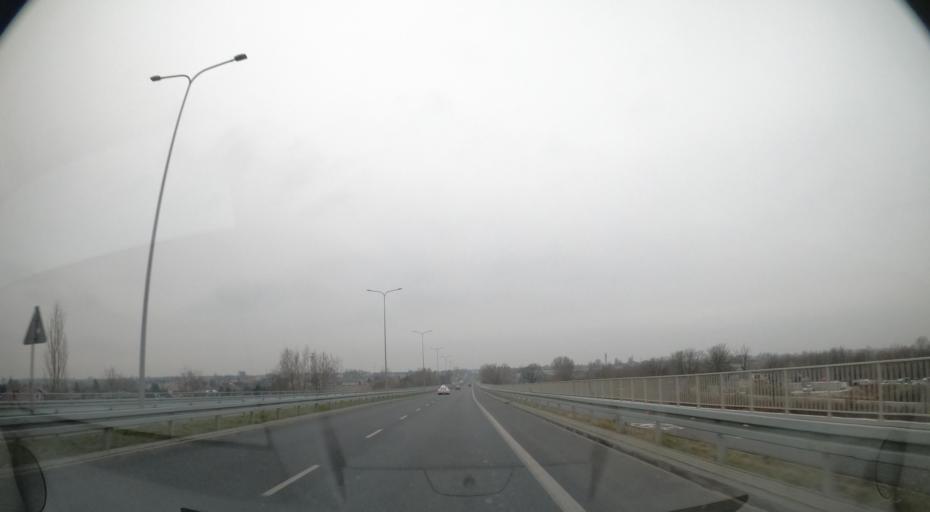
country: PL
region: Masovian Voivodeship
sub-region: Radom
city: Radom
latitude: 51.4075
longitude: 21.2026
